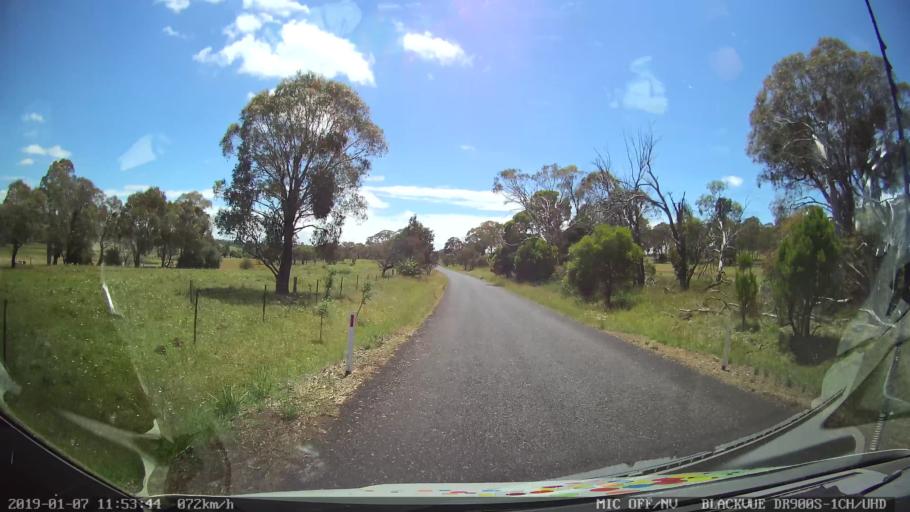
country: AU
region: New South Wales
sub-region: Guyra
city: Guyra
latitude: -30.3025
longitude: 151.6605
